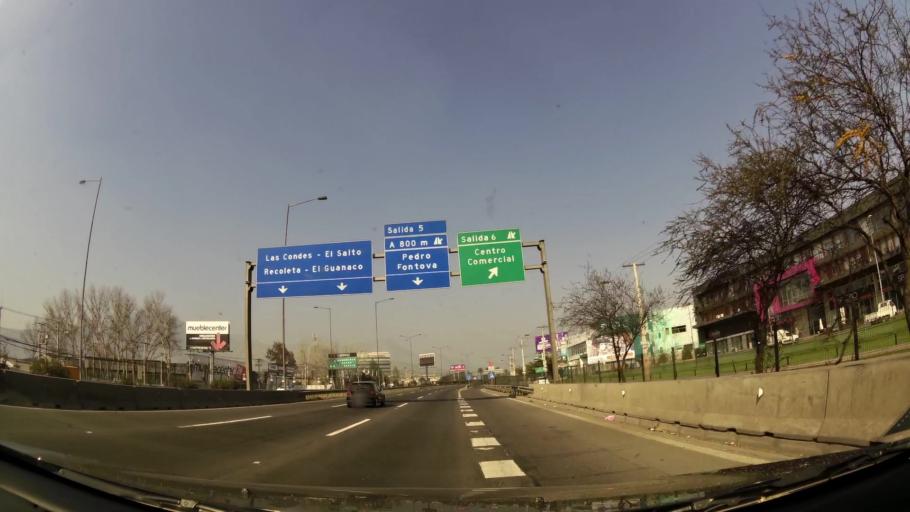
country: CL
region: Santiago Metropolitan
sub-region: Provincia de Santiago
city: Lo Prado
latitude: -33.3668
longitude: -70.6841
